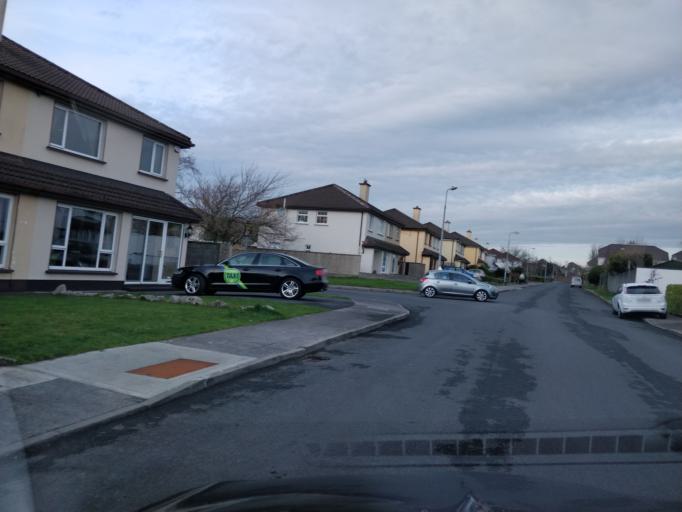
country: IE
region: Connaught
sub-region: County Galway
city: Bearna
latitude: 53.2641
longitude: -9.1101
